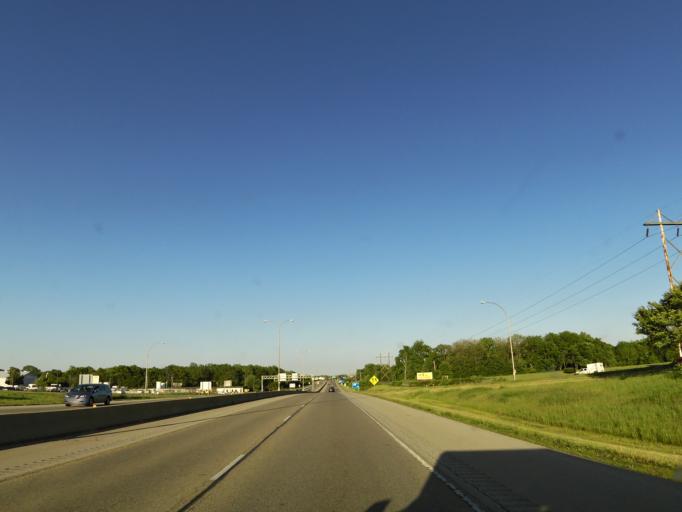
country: US
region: Illinois
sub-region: Champaign County
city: Urbana
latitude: 40.1350
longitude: -88.2185
